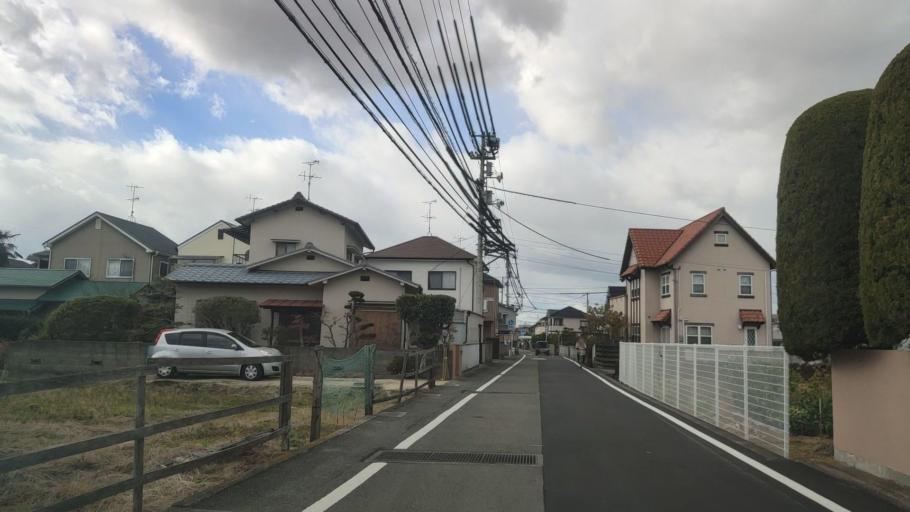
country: JP
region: Ehime
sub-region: Shikoku-chuo Shi
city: Matsuyama
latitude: 33.8097
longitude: 132.7879
